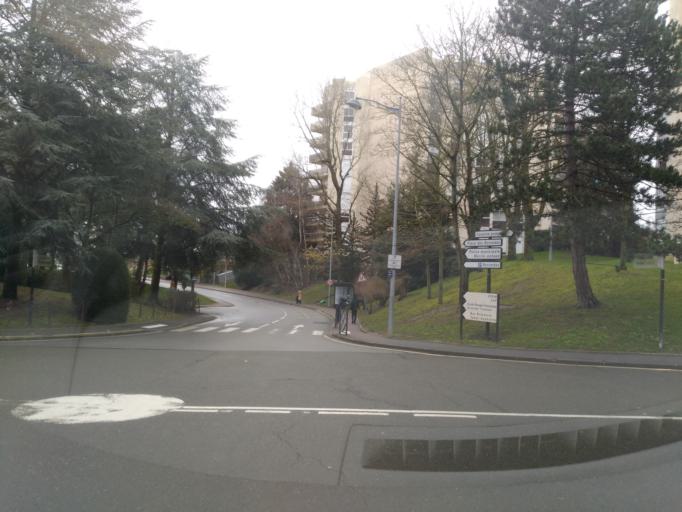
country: FR
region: Ile-de-France
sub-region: Departement des Yvelines
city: Fourqueux
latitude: 48.8938
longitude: 2.0670
